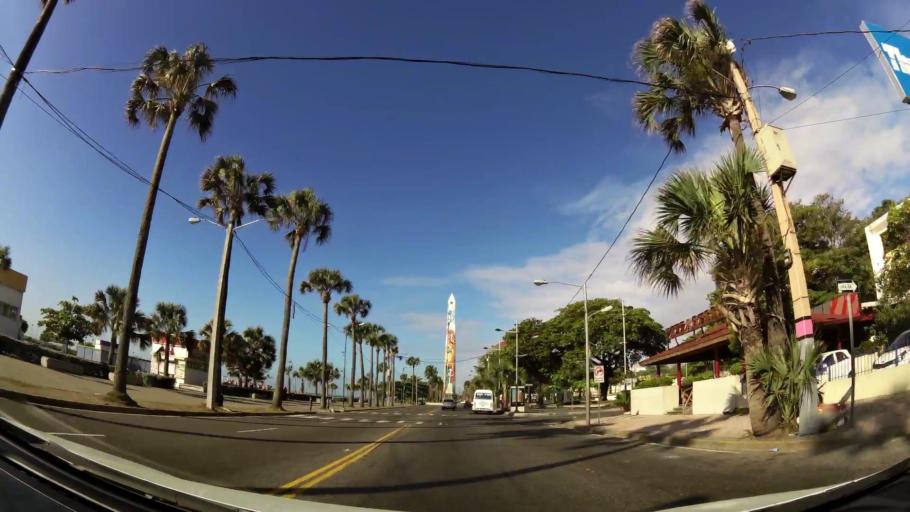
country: DO
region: Nacional
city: Ciudad Nueva
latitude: 18.4653
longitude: -69.8928
